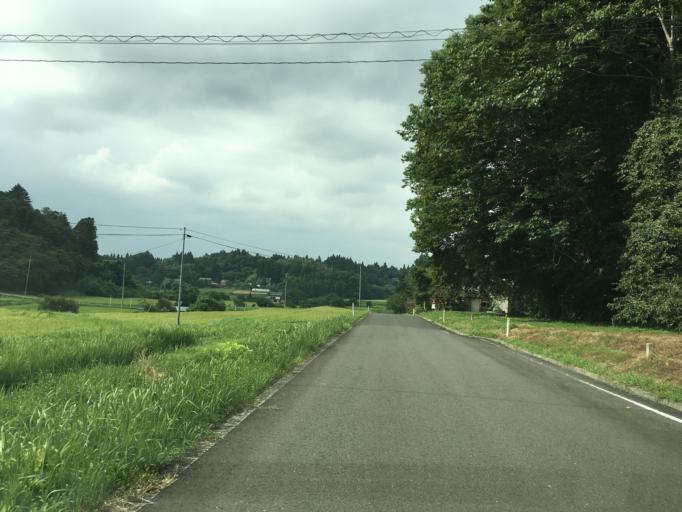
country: JP
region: Iwate
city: Ichinoseki
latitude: 38.8711
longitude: 141.3641
